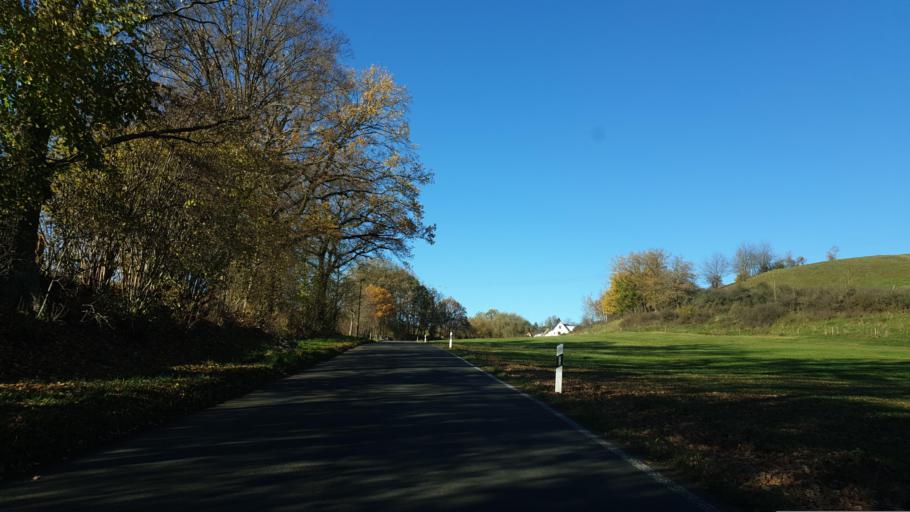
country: DE
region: Saxony
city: Elsterberg
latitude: 50.6075
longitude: 12.1426
